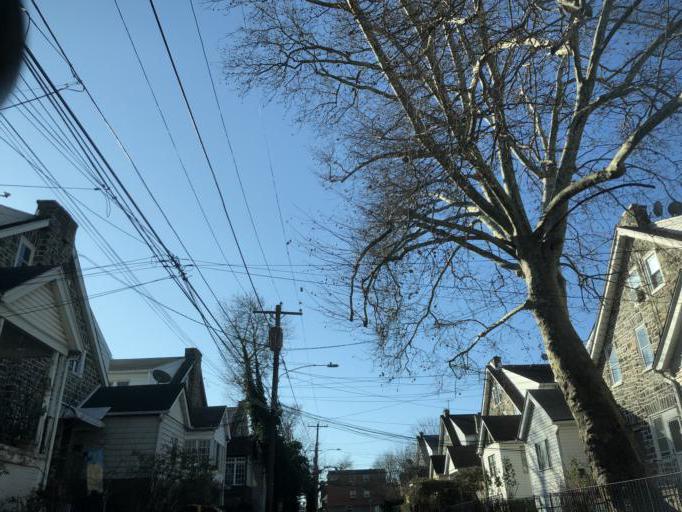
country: US
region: Pennsylvania
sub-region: Delaware County
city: Millbourne
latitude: 39.9601
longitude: -75.2593
